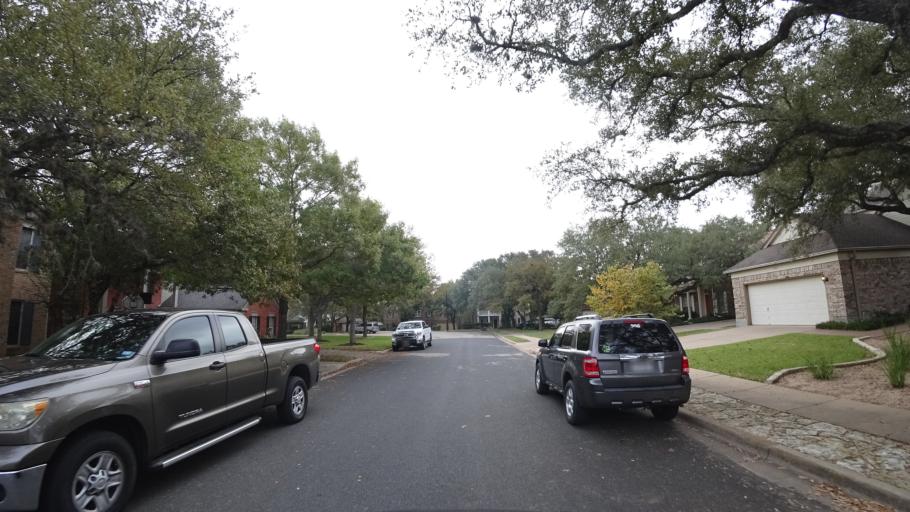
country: US
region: Texas
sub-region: Travis County
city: Shady Hollow
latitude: 30.1909
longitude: -97.8924
